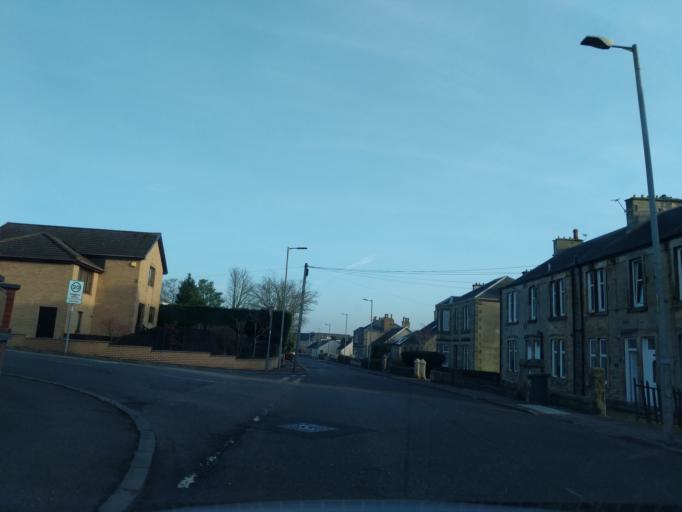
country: GB
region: Scotland
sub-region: South Lanarkshire
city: Carluke
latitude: 55.7357
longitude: -3.8463
